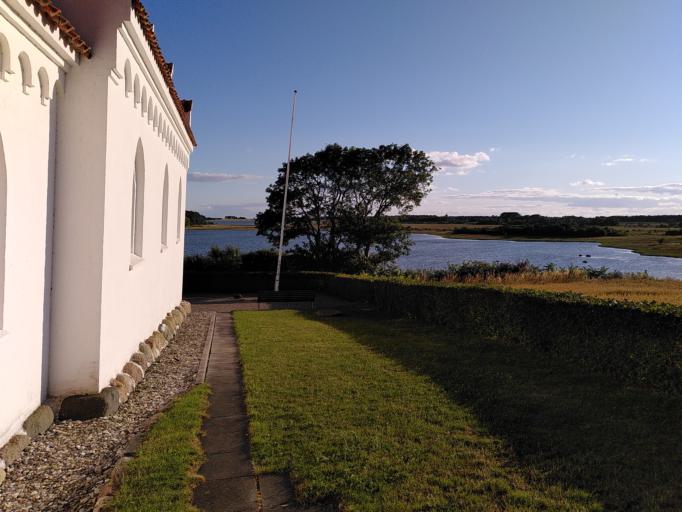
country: DK
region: Central Jutland
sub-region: Samso Kommune
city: Tranebjerg
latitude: 55.9189
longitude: 10.6336
